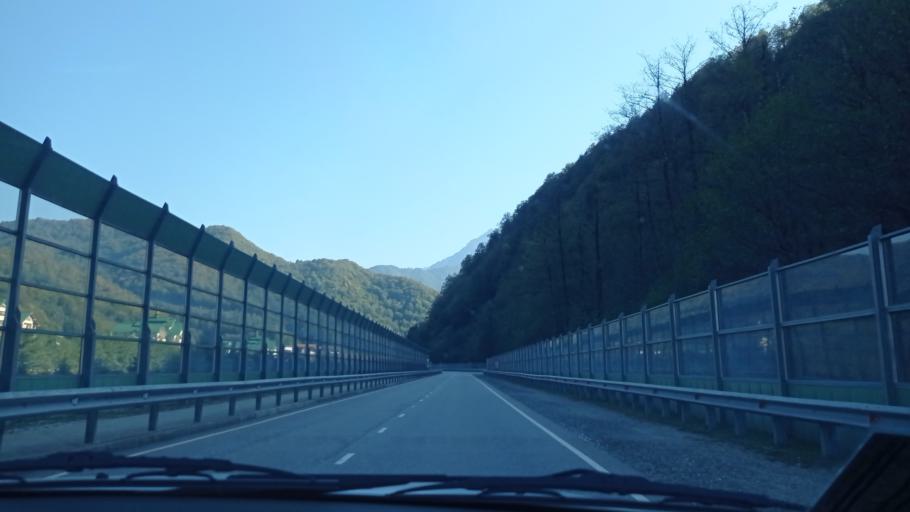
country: RU
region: Krasnodarskiy
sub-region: Sochi City
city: Krasnaya Polyana
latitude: 43.6931
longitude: 40.2699
